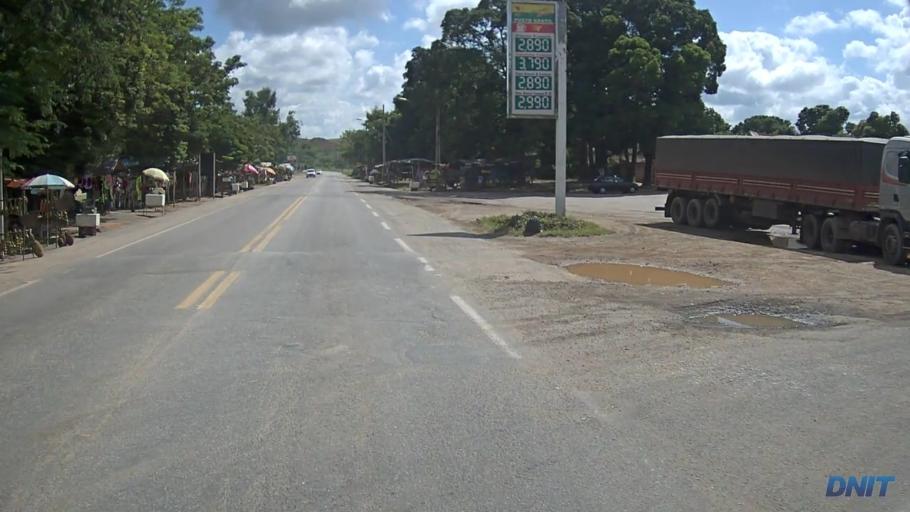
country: BR
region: Minas Gerais
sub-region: Belo Oriente
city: Belo Oriente
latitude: -19.1545
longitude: -42.2361
